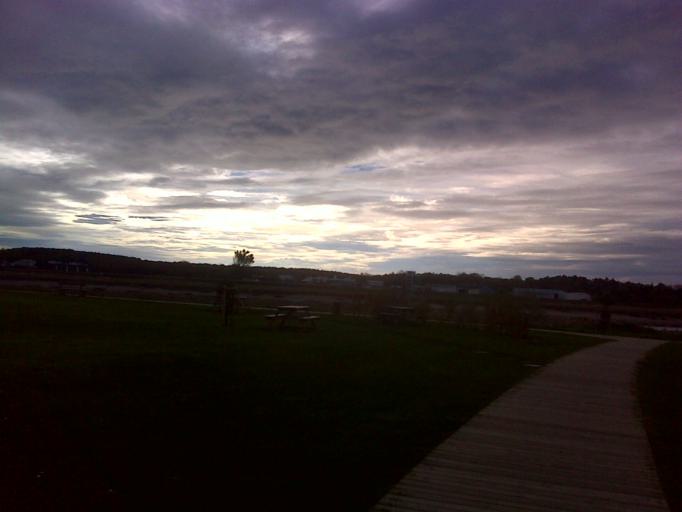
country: FR
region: Nord-Pas-de-Calais
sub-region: Departement du Pas-de-Calais
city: Etaples
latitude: 50.5201
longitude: 1.6275
